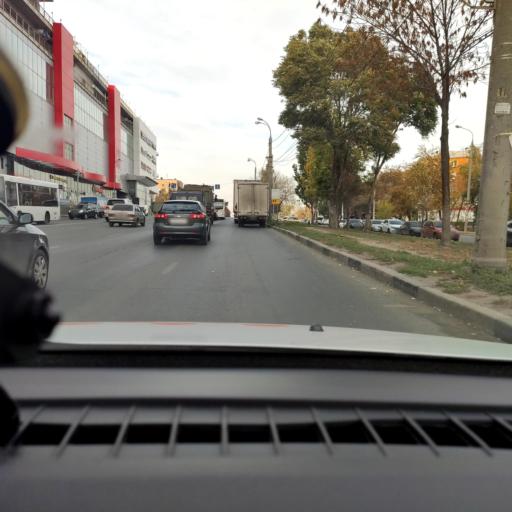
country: RU
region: Samara
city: Samara
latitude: 53.1897
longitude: 50.1912
